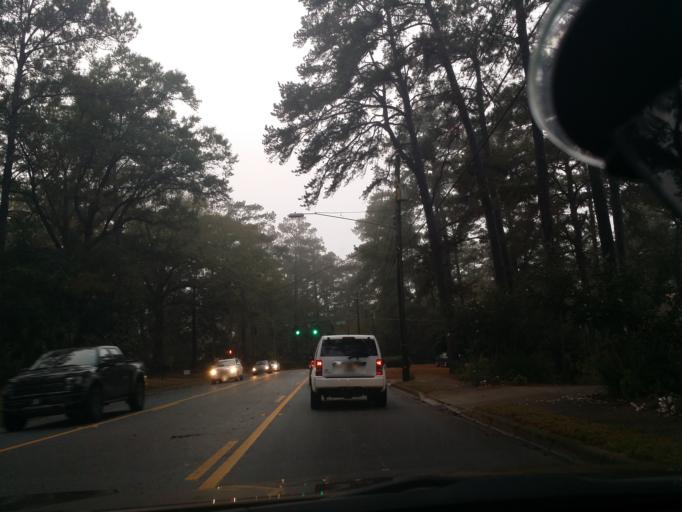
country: US
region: Florida
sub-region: Leon County
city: Tallahassee
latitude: 30.4645
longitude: -84.2633
